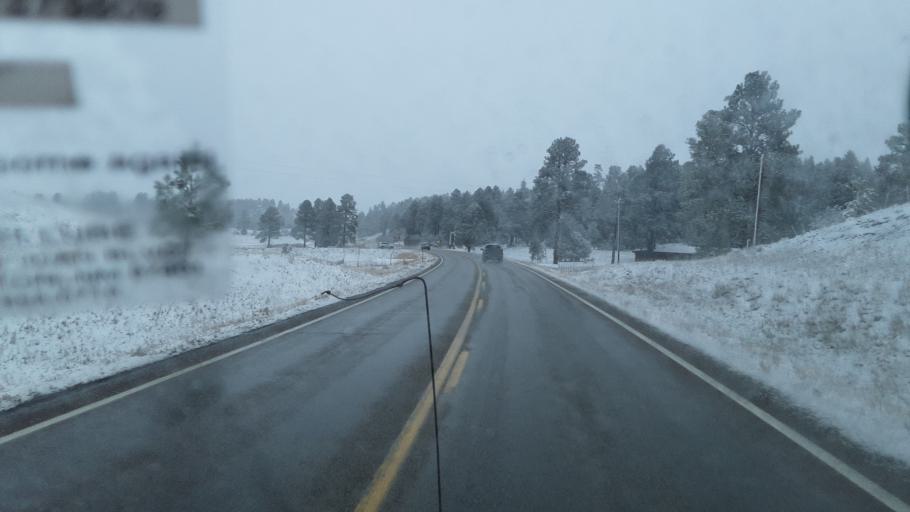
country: US
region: Colorado
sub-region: Archuleta County
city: Pagosa Springs
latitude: 37.2027
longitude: -106.9644
